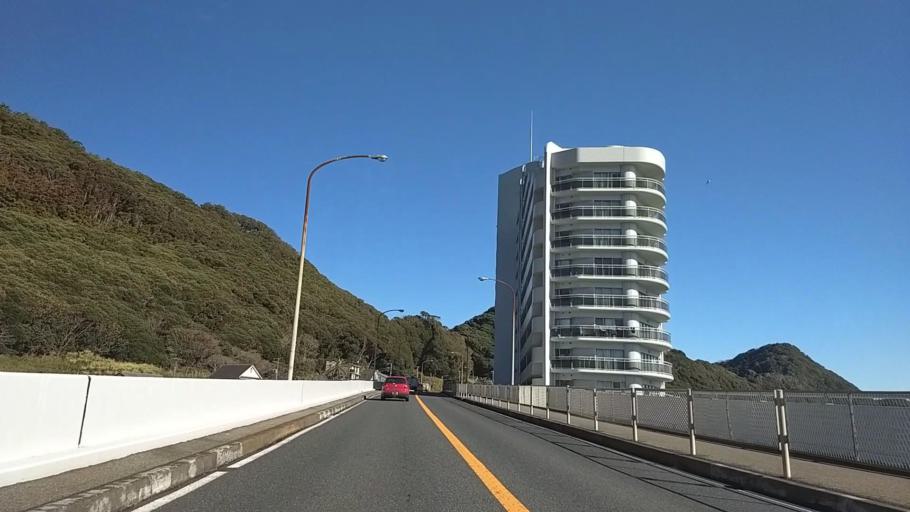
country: JP
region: Chiba
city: Kawaguchi
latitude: 35.1224
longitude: 140.1336
